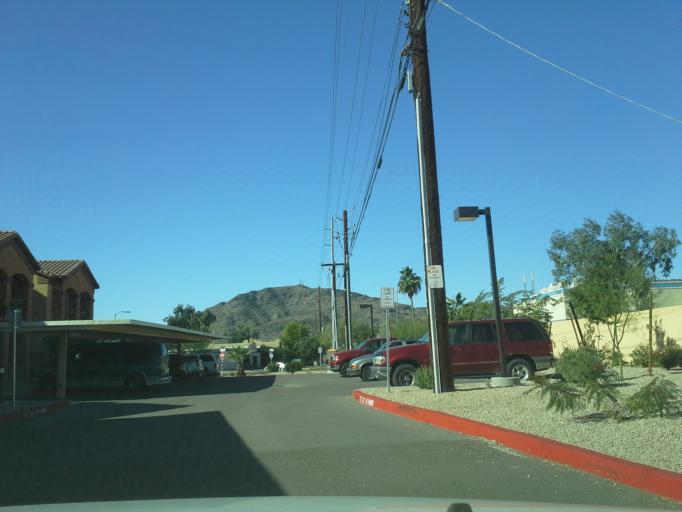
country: US
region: Arizona
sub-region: Maricopa County
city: Paradise Valley
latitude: 33.5858
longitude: -112.0483
